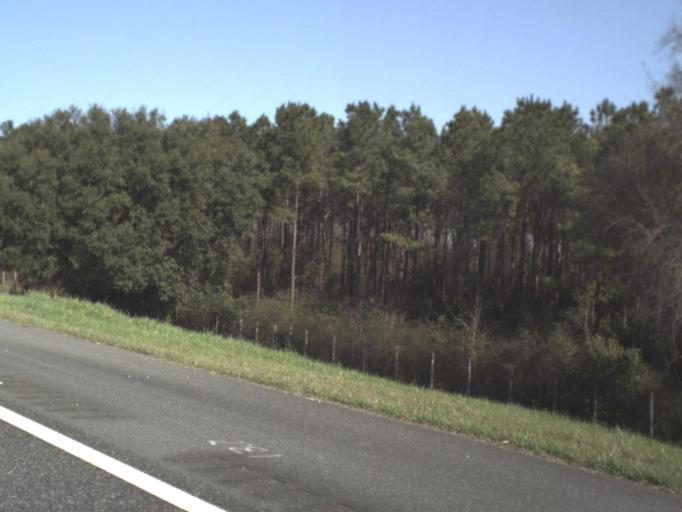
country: US
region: Florida
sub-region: Leon County
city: Tallahassee
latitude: 30.4967
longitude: -84.1757
